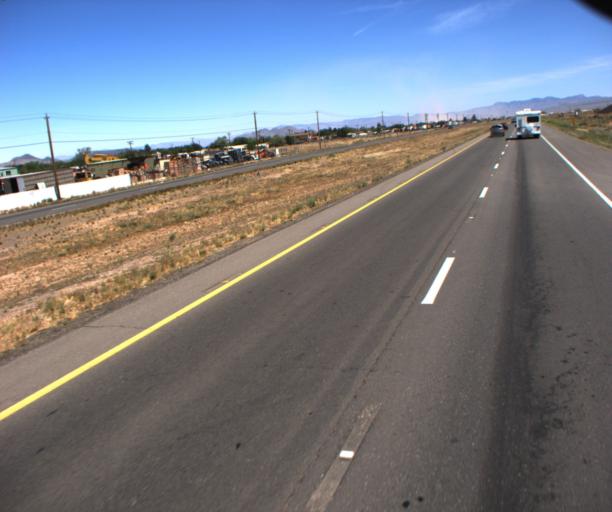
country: US
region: Arizona
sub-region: Mohave County
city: New Kingman-Butler
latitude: 35.2399
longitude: -113.9887
